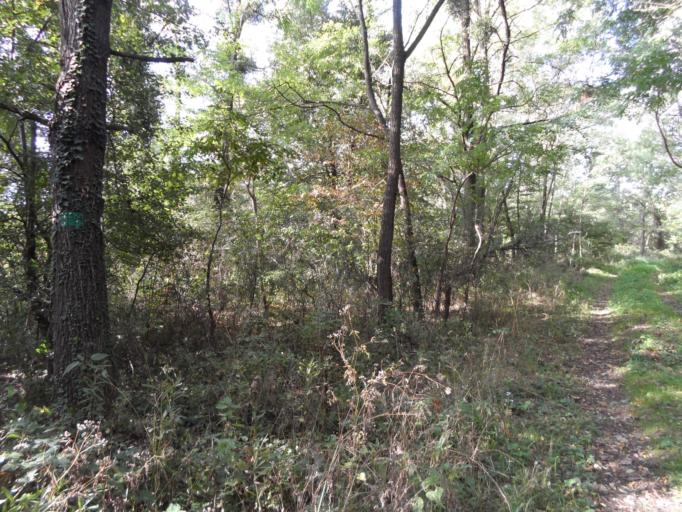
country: HU
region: Veszprem
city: Devecser
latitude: 47.2048
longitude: 17.4562
